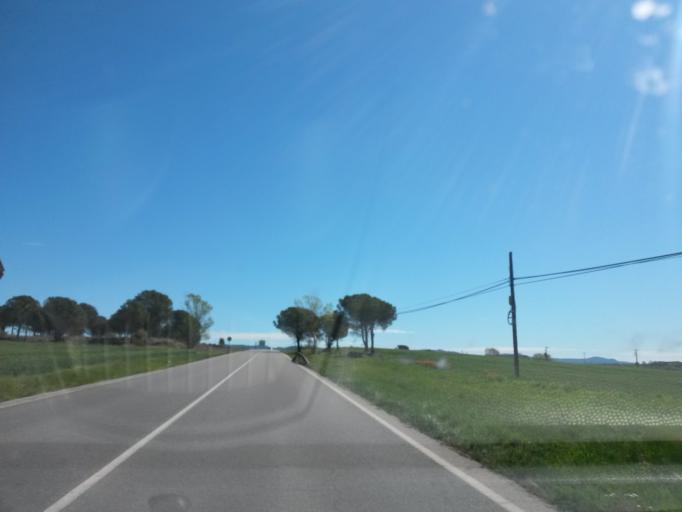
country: ES
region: Catalonia
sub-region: Provincia de Girona
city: Riudellots de la Selva
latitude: 41.8908
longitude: 2.7862
